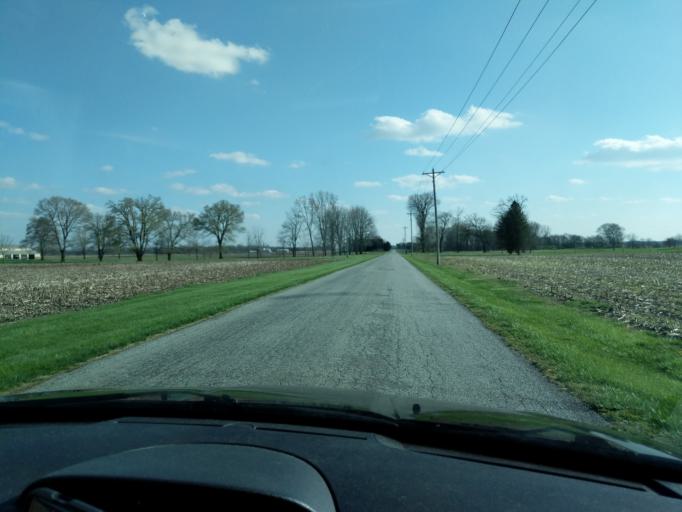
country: US
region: Ohio
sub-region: Champaign County
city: Urbana
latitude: 40.1533
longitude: -83.8144
